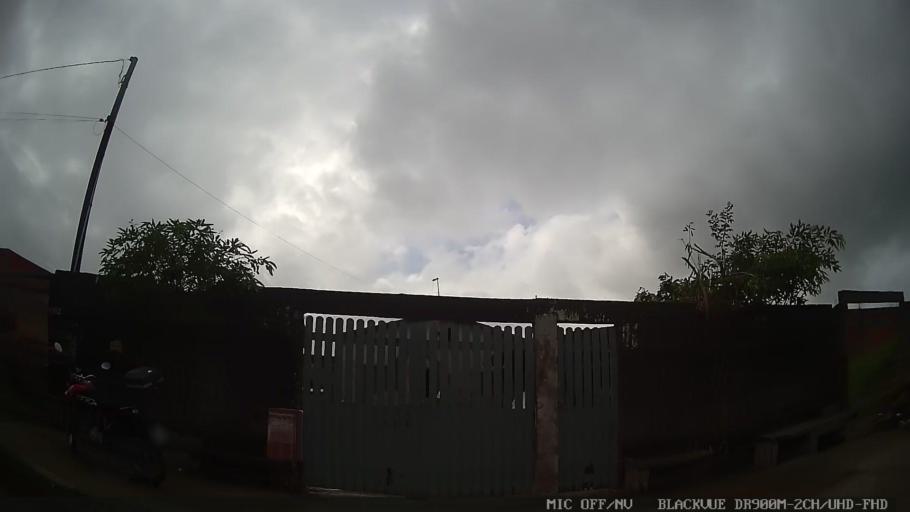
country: BR
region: Sao Paulo
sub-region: Itanhaem
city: Itanhaem
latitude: -24.1965
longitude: -46.8315
